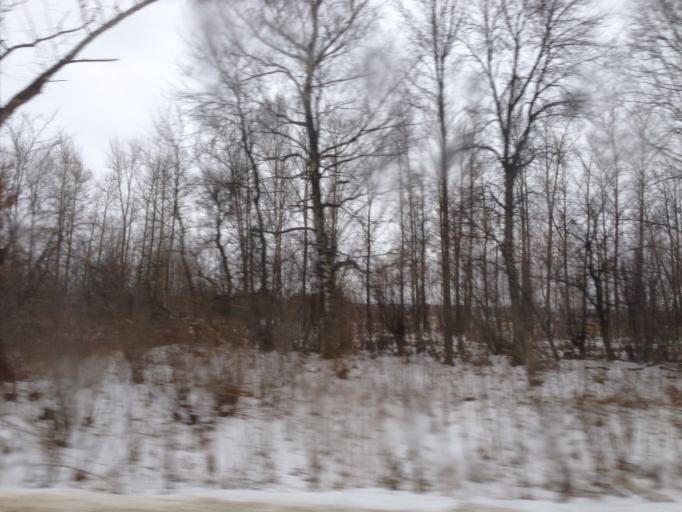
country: RU
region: Tula
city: Uzlovaya
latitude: 54.0008
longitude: 38.1223
